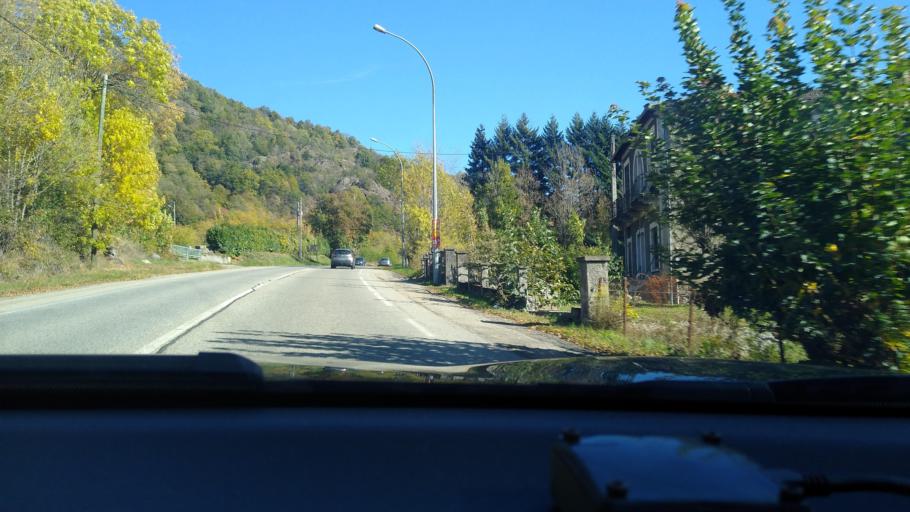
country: FR
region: Midi-Pyrenees
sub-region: Departement de l'Ariege
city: Ax-les-Thermes
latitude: 42.7297
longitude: 1.8217
